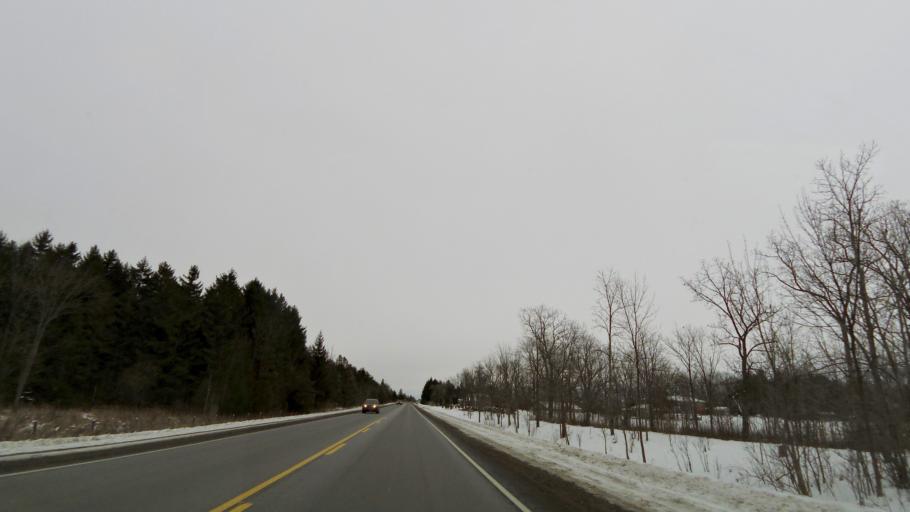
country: CA
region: Ontario
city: Cambridge
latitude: 43.3079
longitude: -80.1483
